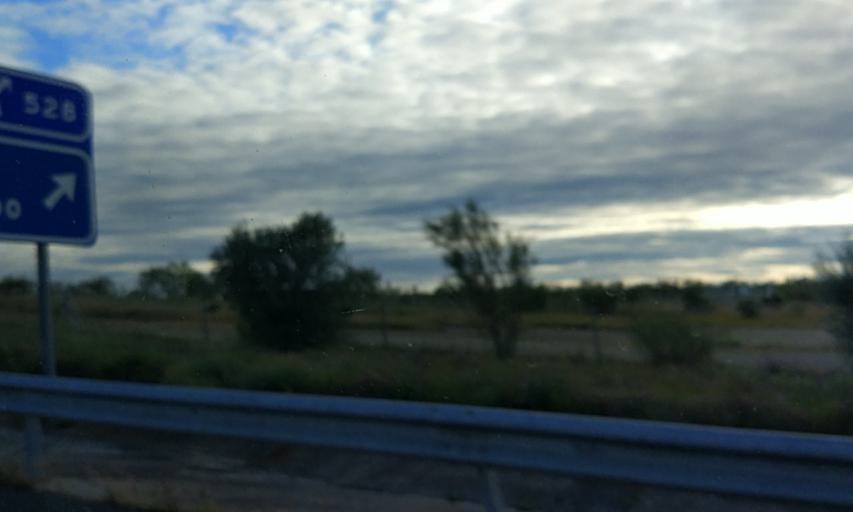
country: ES
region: Extremadura
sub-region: Provincia de Caceres
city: Santiago del Campo
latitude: 39.6618
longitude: -6.3927
